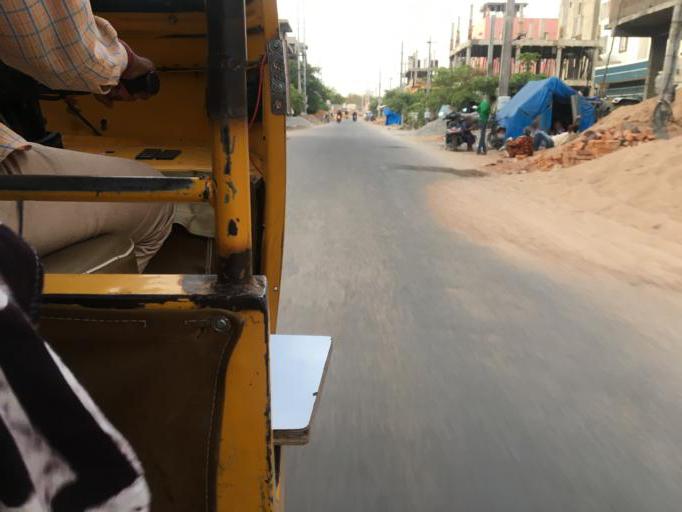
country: IN
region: Telangana
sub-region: Medak
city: Serilingampalle
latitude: 17.4340
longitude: 78.3347
